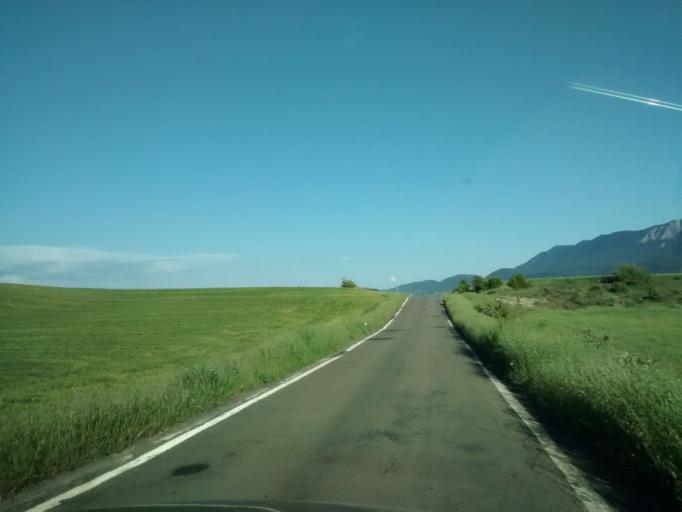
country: ES
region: Aragon
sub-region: Provincia de Huesca
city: Jaca
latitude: 42.5861
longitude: -0.6026
